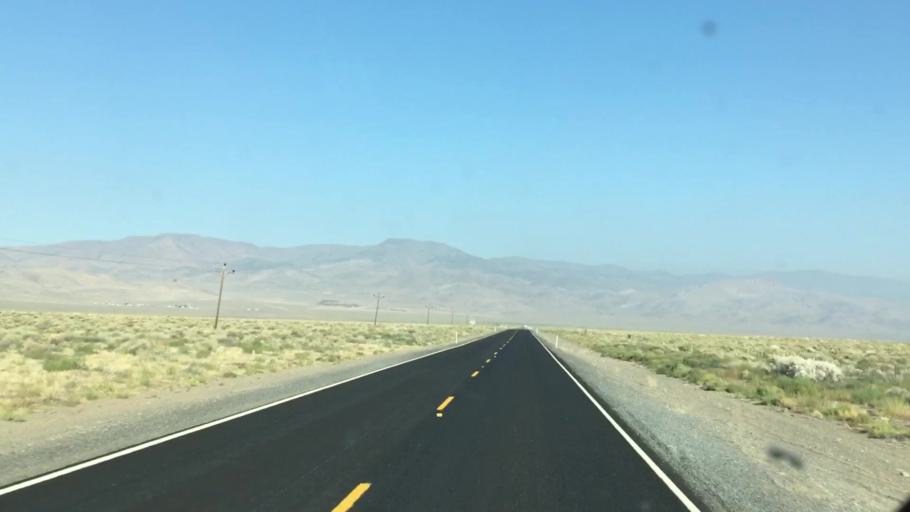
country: US
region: Nevada
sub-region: Lyon County
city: Fernley
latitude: 39.6437
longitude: -119.3060
